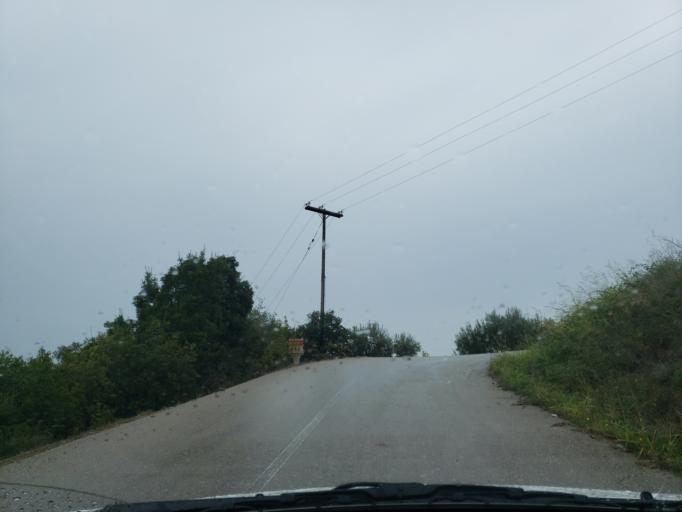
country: GR
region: Central Greece
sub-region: Nomos Fthiotidos
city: Anthili
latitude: 38.7955
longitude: 22.4837
